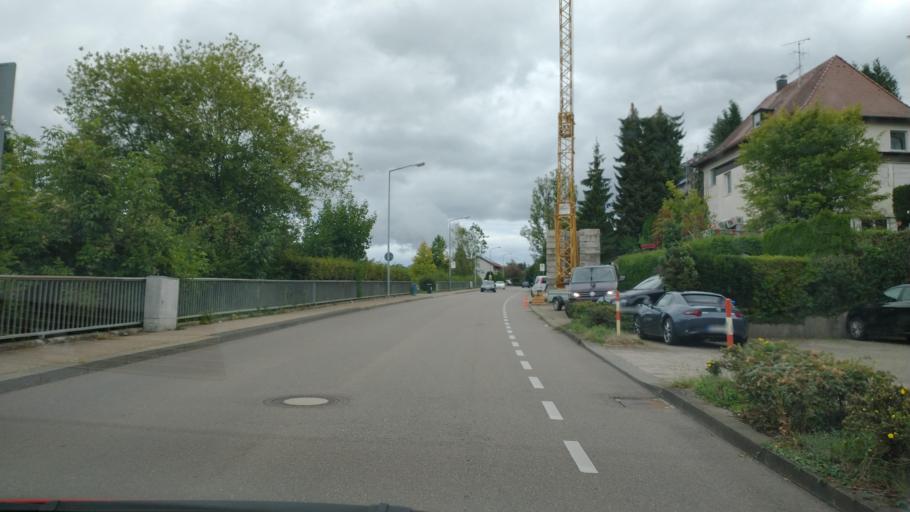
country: DE
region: Baden-Wuerttemberg
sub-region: Regierungsbezirk Stuttgart
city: Schwabisch Gmund
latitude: 48.7979
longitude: 9.8098
